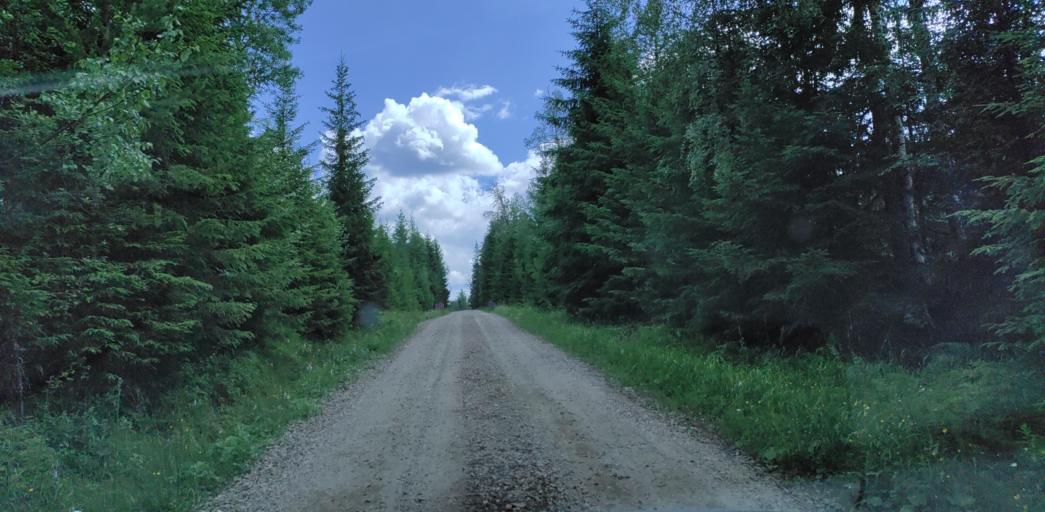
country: SE
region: Vaermland
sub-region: Hagfors Kommun
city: Ekshaerad
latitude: 60.0912
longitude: 13.3418
